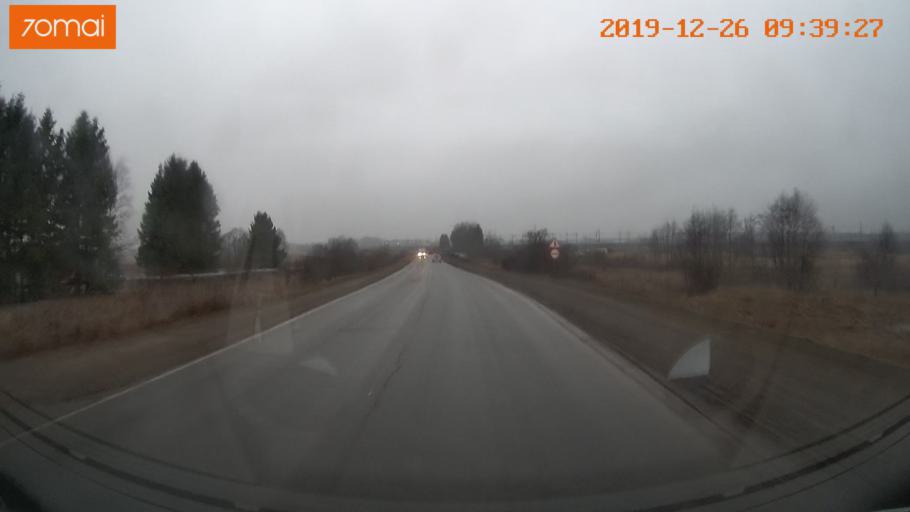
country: RU
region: Vologda
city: Vologda
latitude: 59.1544
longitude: 40.0242
